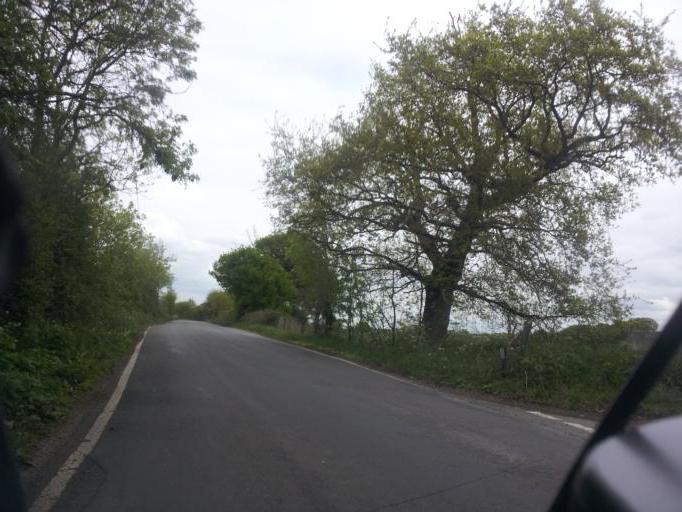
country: GB
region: England
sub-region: Kent
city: Newington
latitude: 51.3755
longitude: 0.6841
